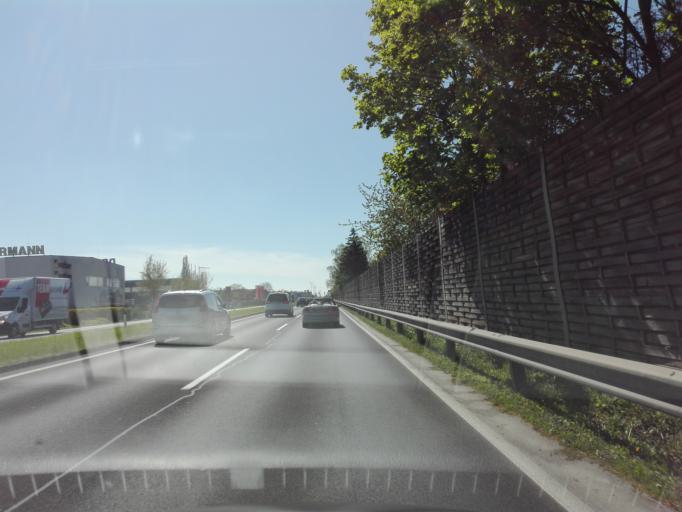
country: AT
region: Upper Austria
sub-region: Politischer Bezirk Linz-Land
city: Traun
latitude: 48.2380
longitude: 14.2418
